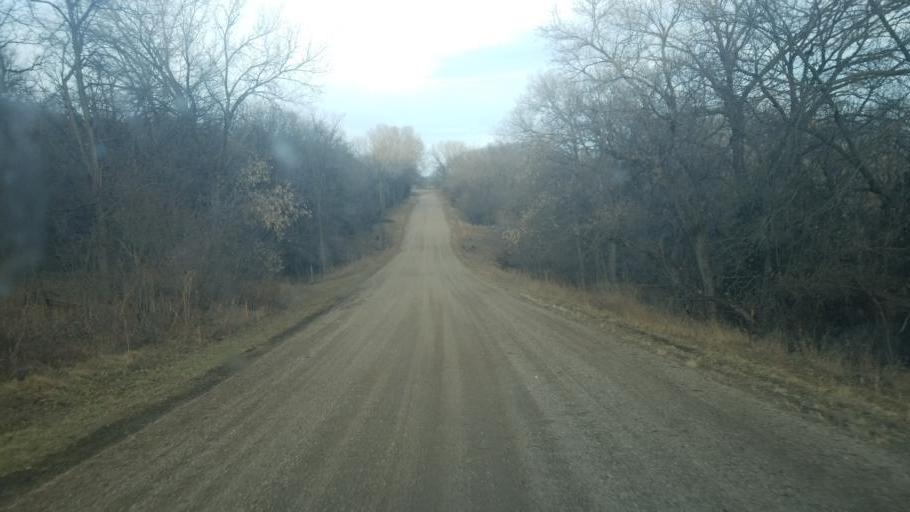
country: US
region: Nebraska
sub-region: Knox County
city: Center
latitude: 42.6861
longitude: -97.8111
